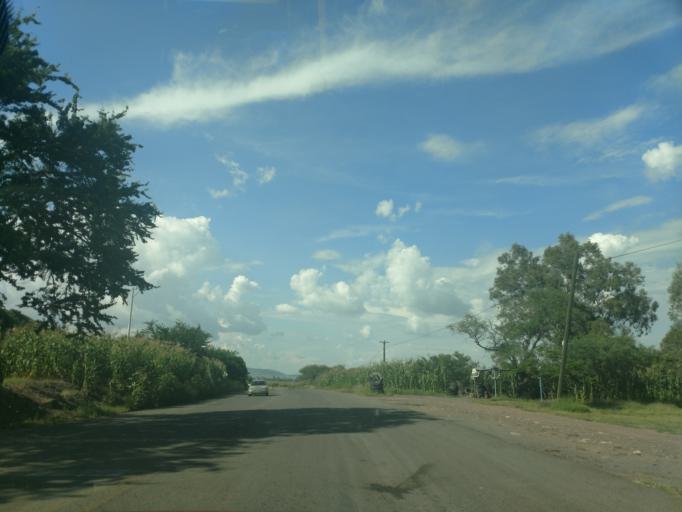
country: MX
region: Jalisco
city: Antonio Escobedo
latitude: 20.8491
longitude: -104.0288
